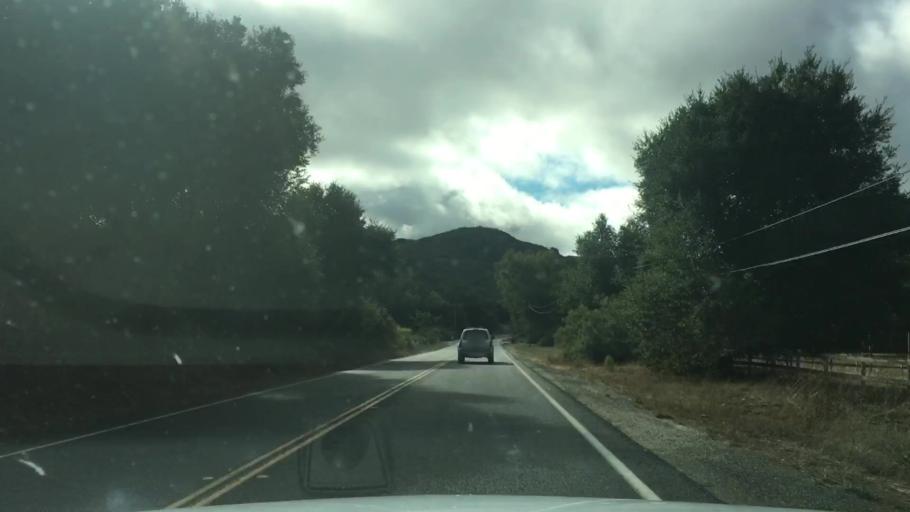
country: US
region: California
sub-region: San Luis Obispo County
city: Atascadero
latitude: 35.4501
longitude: -120.7524
